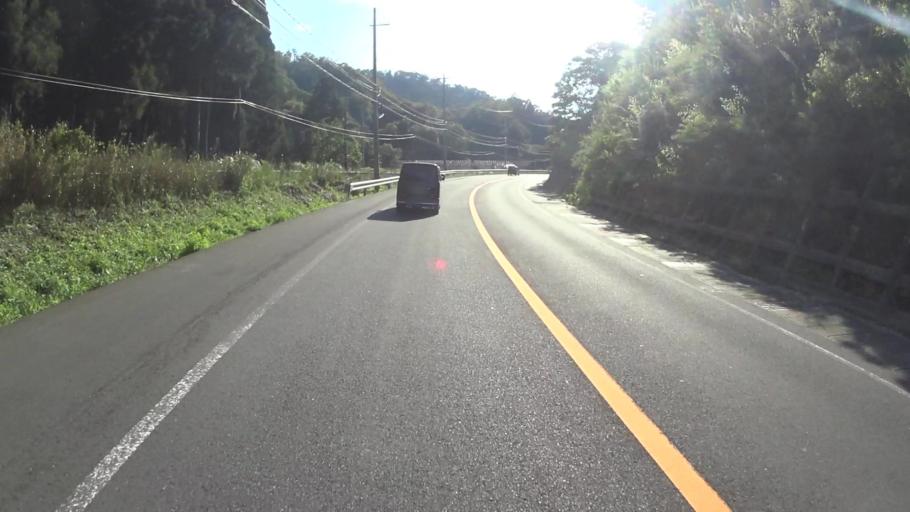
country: JP
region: Kyoto
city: Miyazu
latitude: 35.6599
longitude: 135.0076
